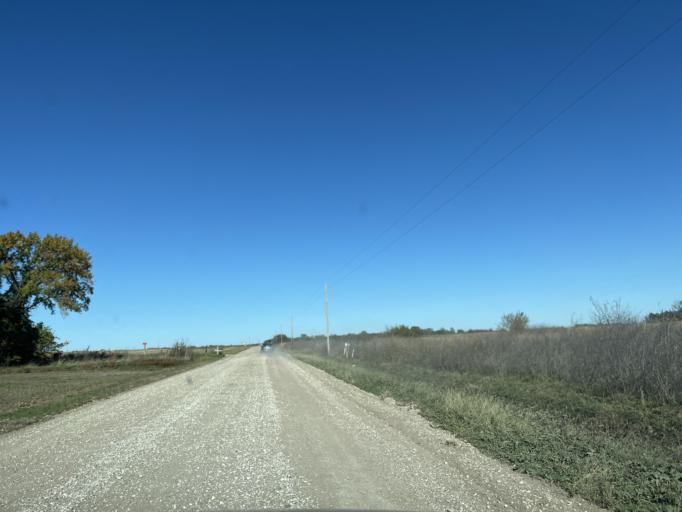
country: US
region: Kansas
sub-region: McPherson County
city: Moundridge
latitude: 38.2188
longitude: -97.6292
